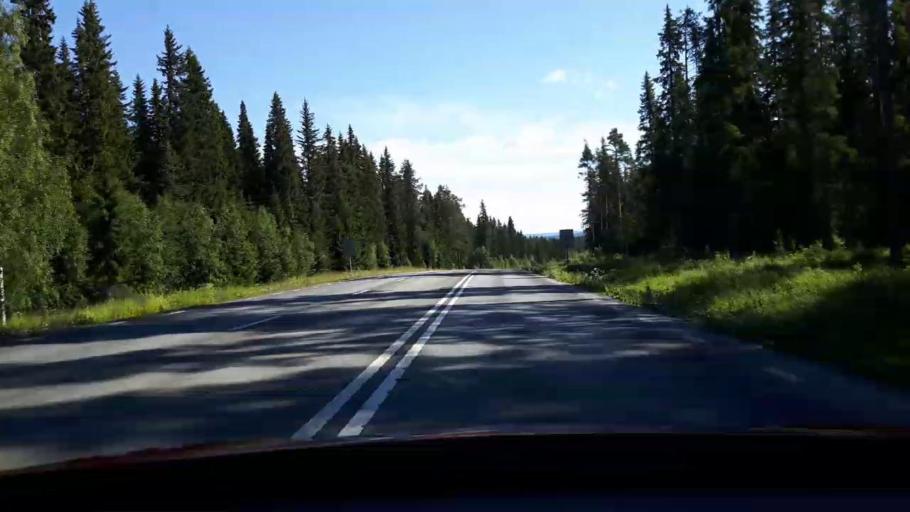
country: SE
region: Jaemtland
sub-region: OEstersunds Kommun
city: Lit
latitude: 63.2450
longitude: 14.7864
